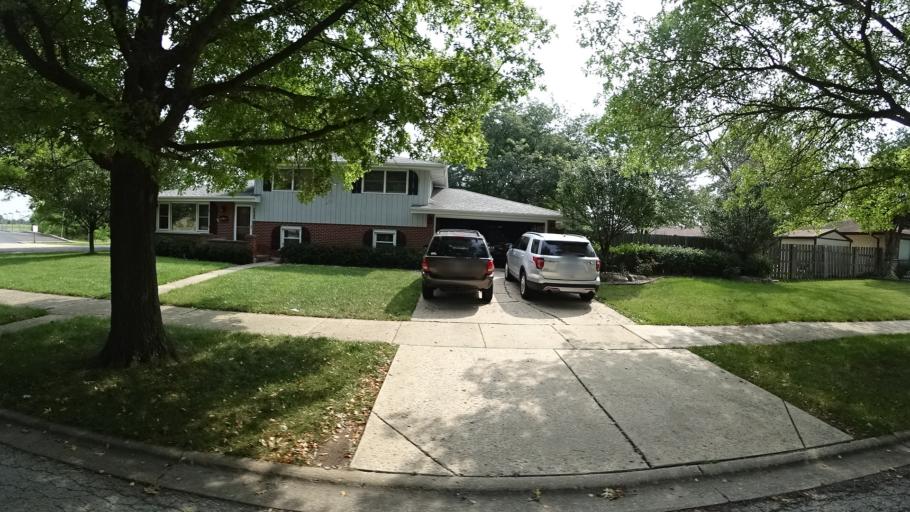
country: US
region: Illinois
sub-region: Cook County
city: Orland Park
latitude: 41.6184
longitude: -87.8619
